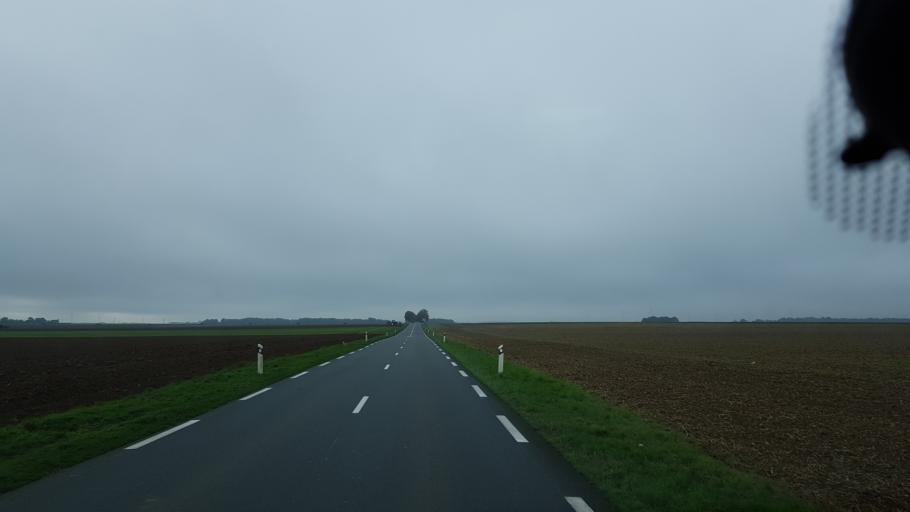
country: FR
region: Ile-de-France
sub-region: Departement de l'Essonne
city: Pussay
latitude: 48.4194
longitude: 1.9649
